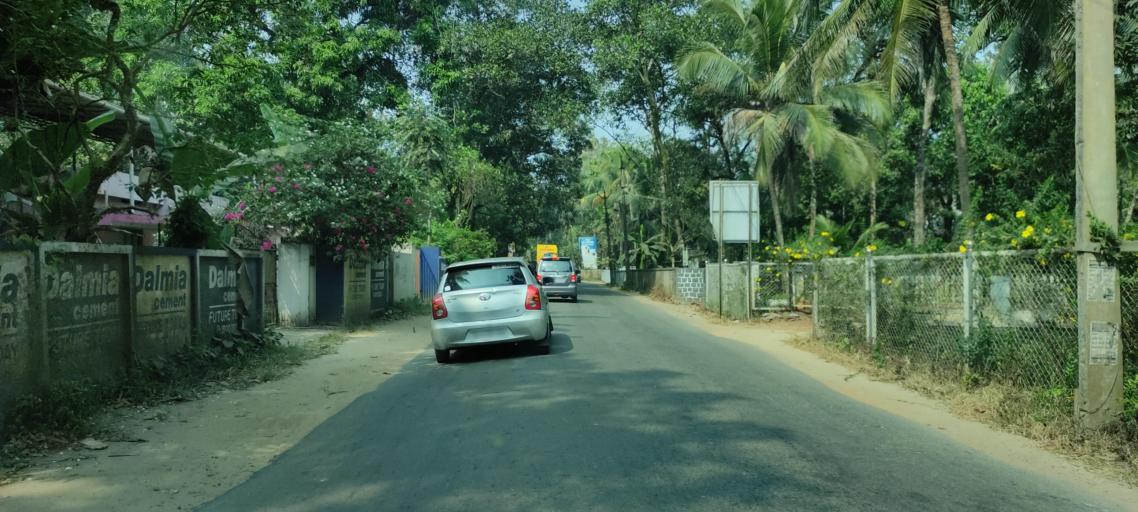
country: IN
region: Kerala
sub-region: Alappuzha
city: Shertallai
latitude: 9.6761
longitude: 76.4211
